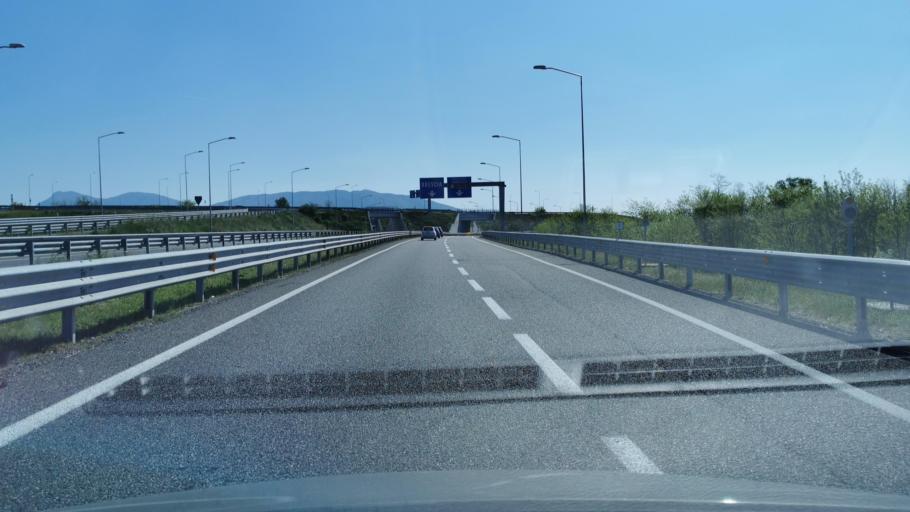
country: IT
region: Lombardy
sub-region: Provincia di Brescia
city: Castegnato
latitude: 45.5479
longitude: 10.1291
